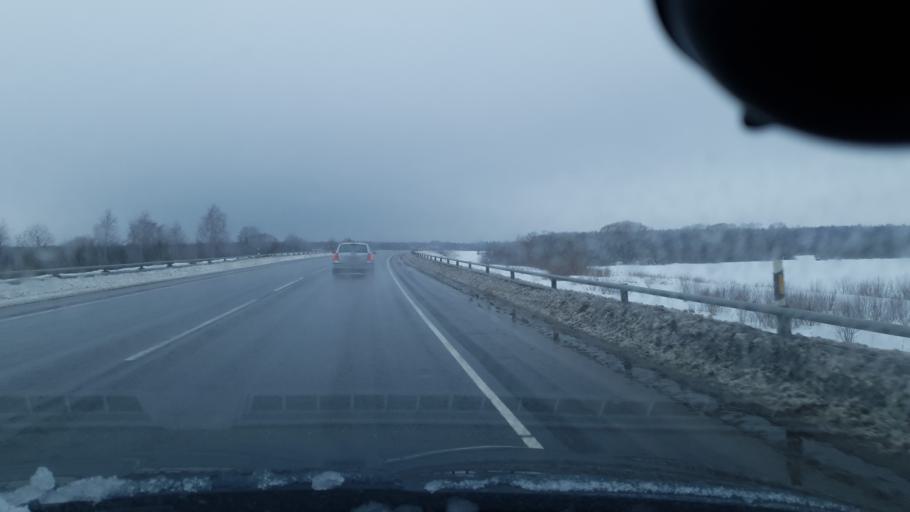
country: EE
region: Tartu
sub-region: Noo vald
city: Noo
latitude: 58.4208
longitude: 26.5113
